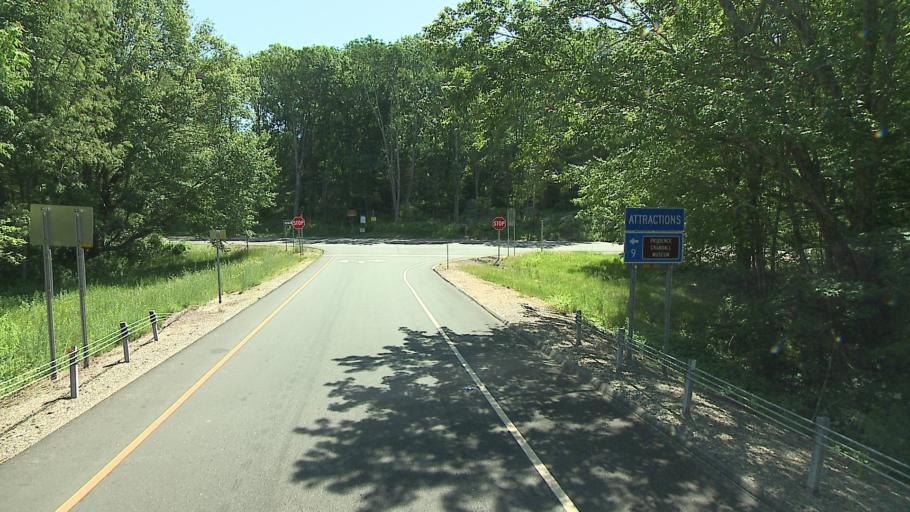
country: US
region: Connecticut
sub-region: New London County
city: Lisbon
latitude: 41.5881
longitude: -72.0231
